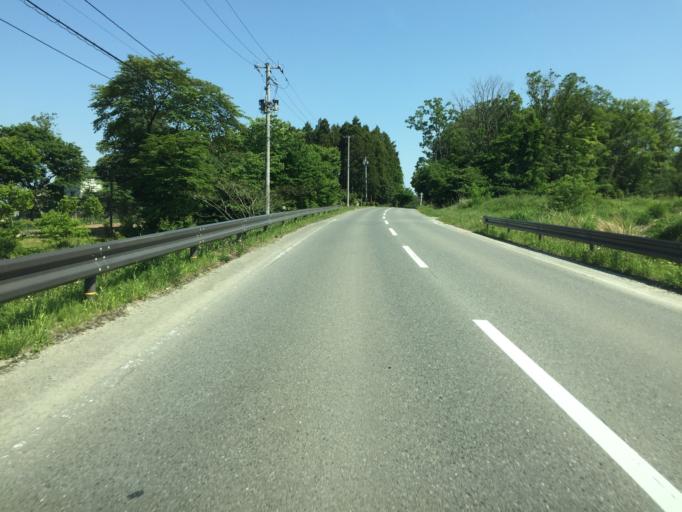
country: JP
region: Miyagi
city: Marumori
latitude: 37.8210
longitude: 140.8784
